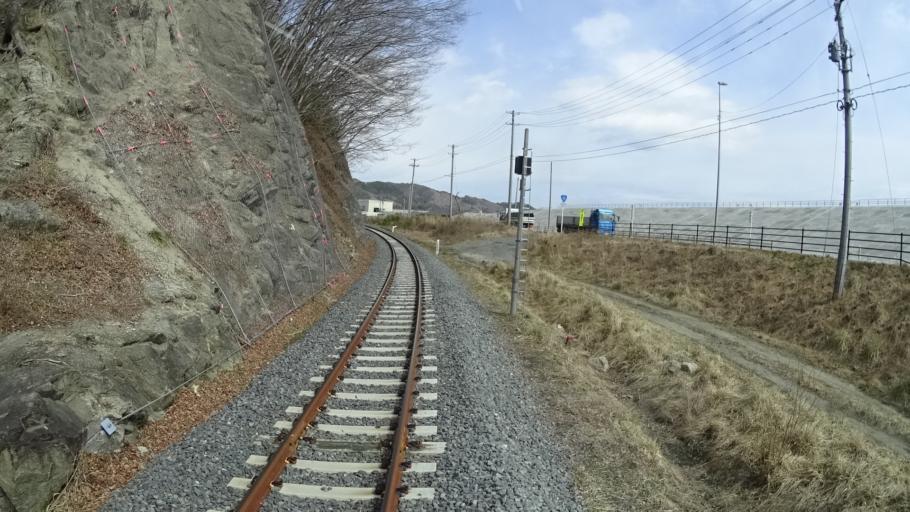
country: JP
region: Iwate
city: Miyako
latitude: 39.5885
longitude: 141.9460
